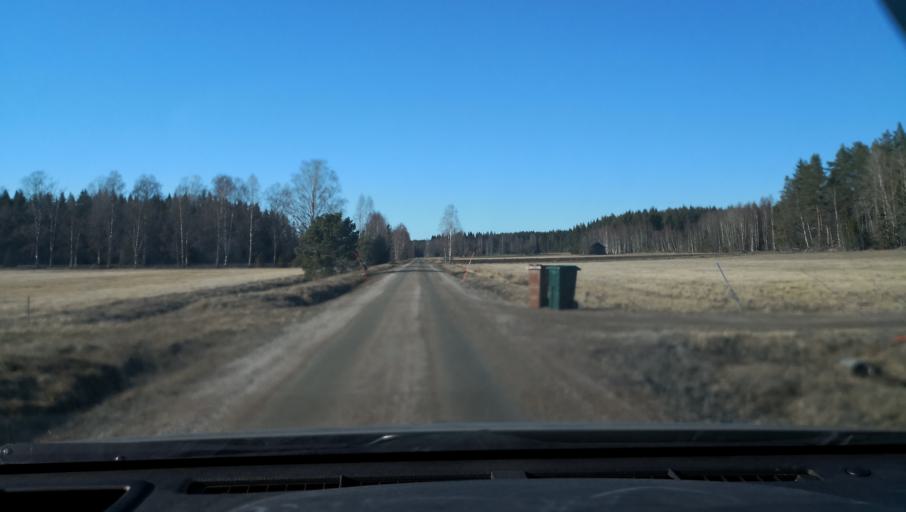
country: SE
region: Vaestmanland
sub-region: Sala Kommun
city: Sala
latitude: 60.1270
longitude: 16.6549
